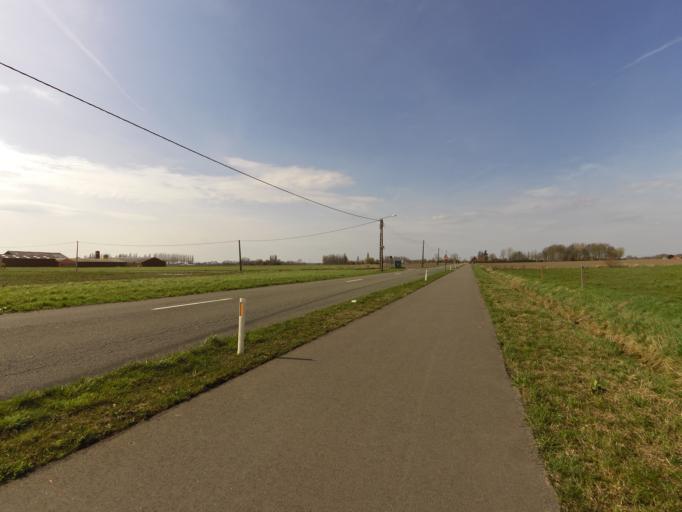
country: BE
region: Flanders
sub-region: Provincie West-Vlaanderen
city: Koekelare
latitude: 51.1031
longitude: 2.9746
